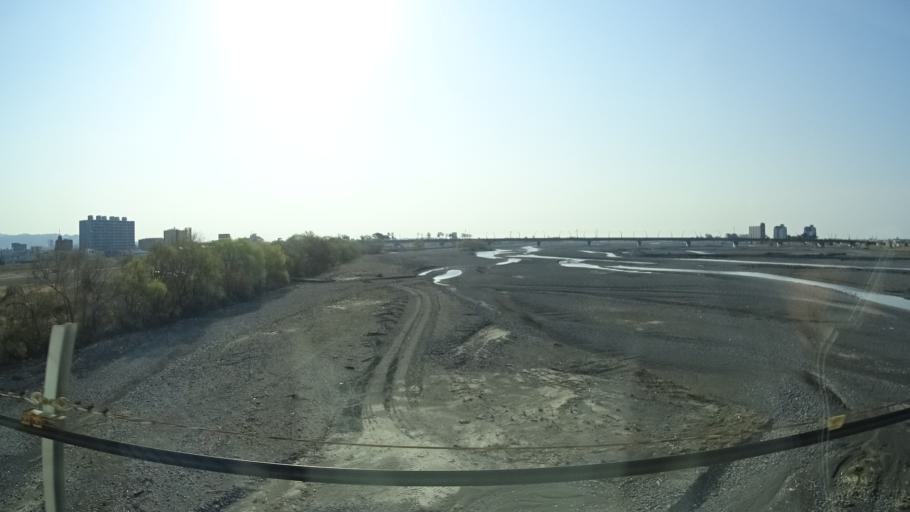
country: JP
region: Shizuoka
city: Shizuoka-shi
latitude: 34.9579
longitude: 138.3727
